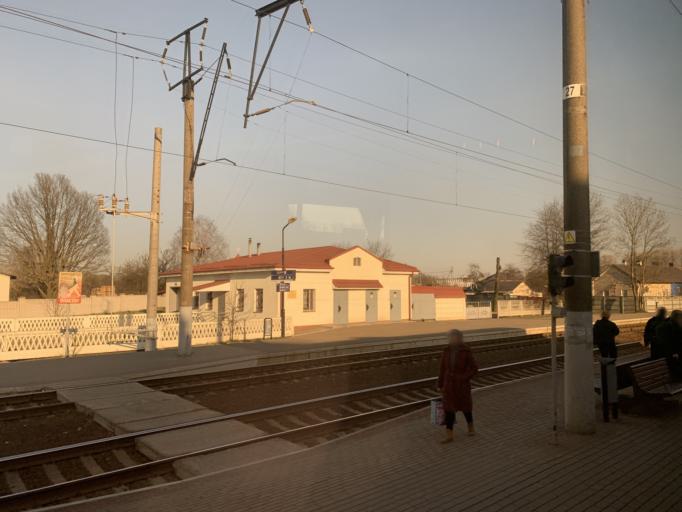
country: BY
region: Minsk
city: Zaslawye
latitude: 54.0087
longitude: 27.2840
